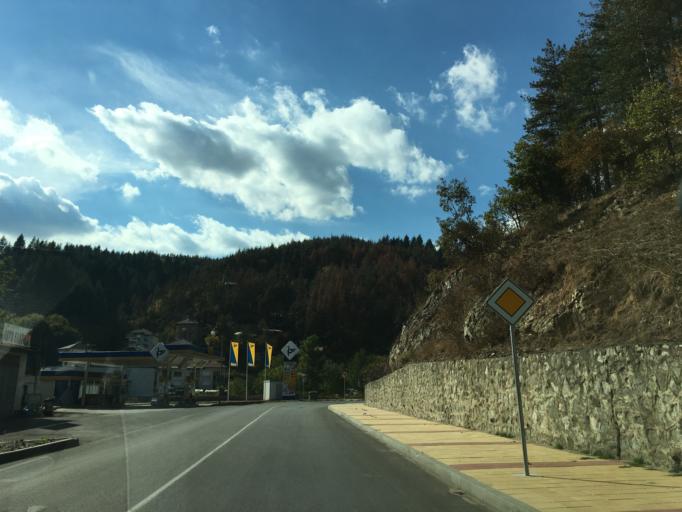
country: BG
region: Smolyan
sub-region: Obshtina Zlatograd
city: Zlatograd
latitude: 41.3919
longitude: 25.0823
